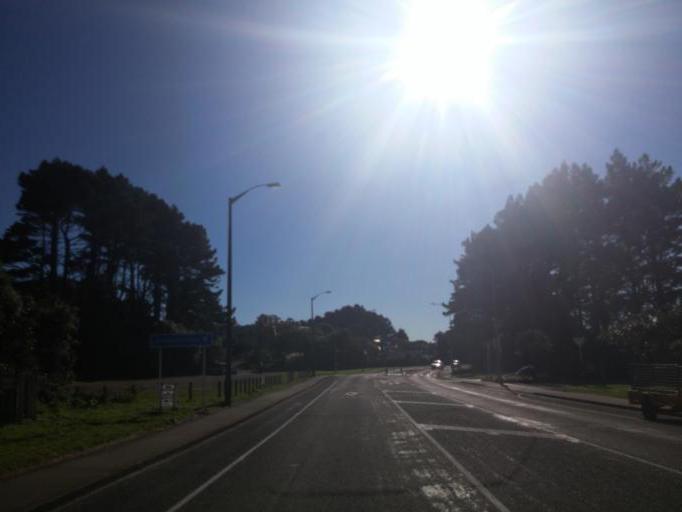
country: NZ
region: Wellington
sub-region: Wellington City
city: Wellington
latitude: -41.2323
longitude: 174.7982
